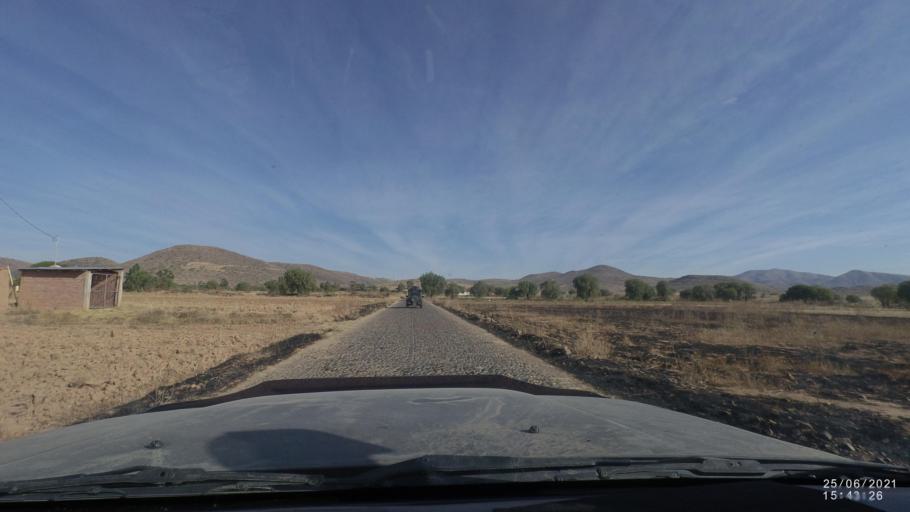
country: BO
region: Cochabamba
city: Cliza
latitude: -17.6482
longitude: -65.9124
